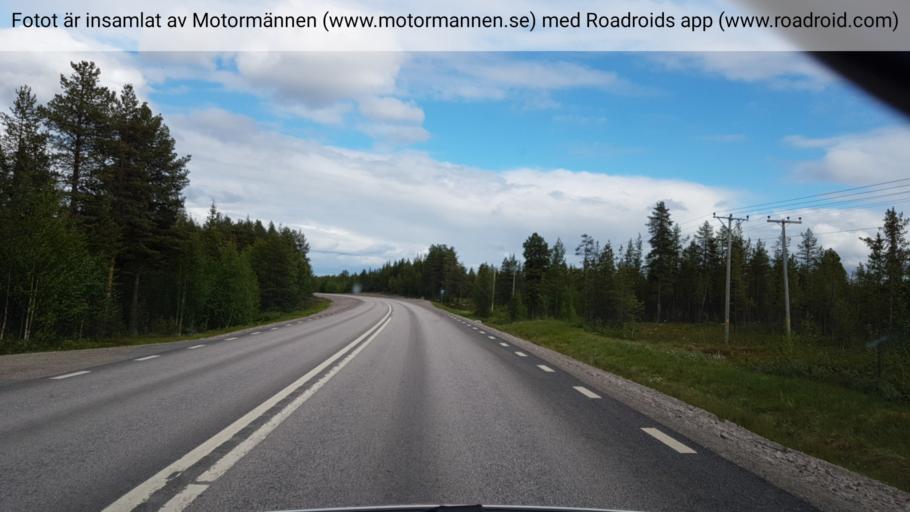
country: SE
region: Norrbotten
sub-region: Gallivare Kommun
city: Malmberget
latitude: 67.6624
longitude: 21.4410
